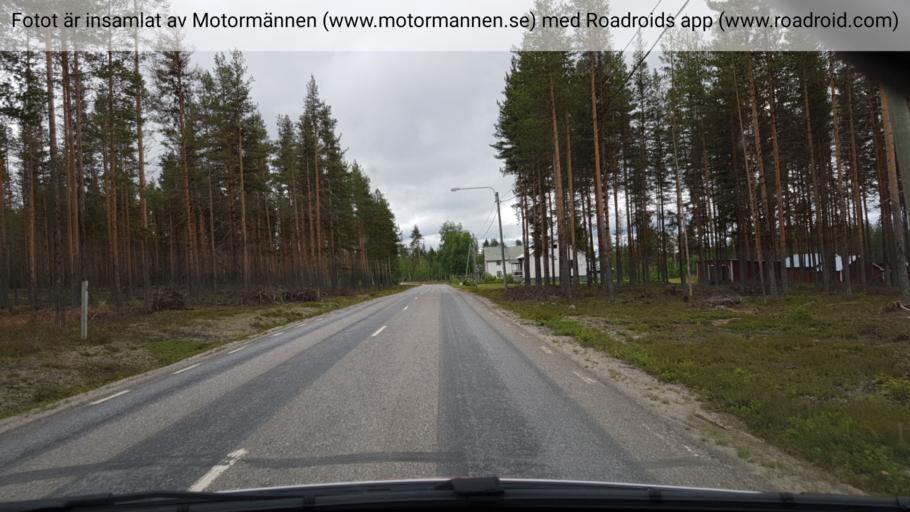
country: SE
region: Vaesterbotten
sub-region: Norsjo Kommun
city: Norsjoe
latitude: 64.6548
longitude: 19.2742
